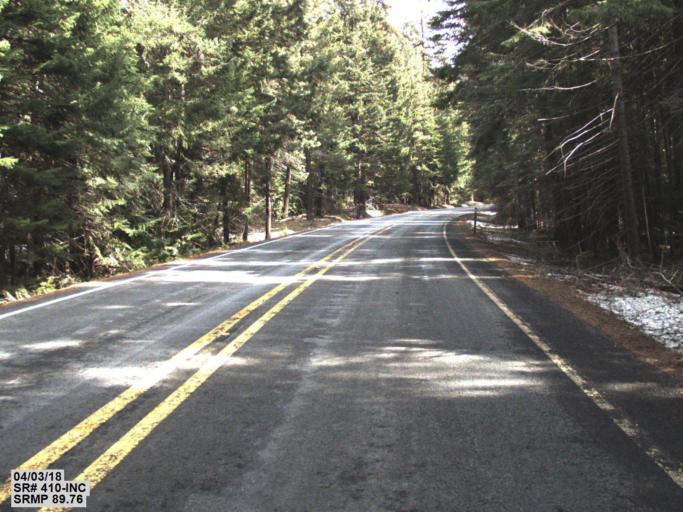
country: US
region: Washington
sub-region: Kittitas County
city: Cle Elum
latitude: 46.9818
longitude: -121.1411
